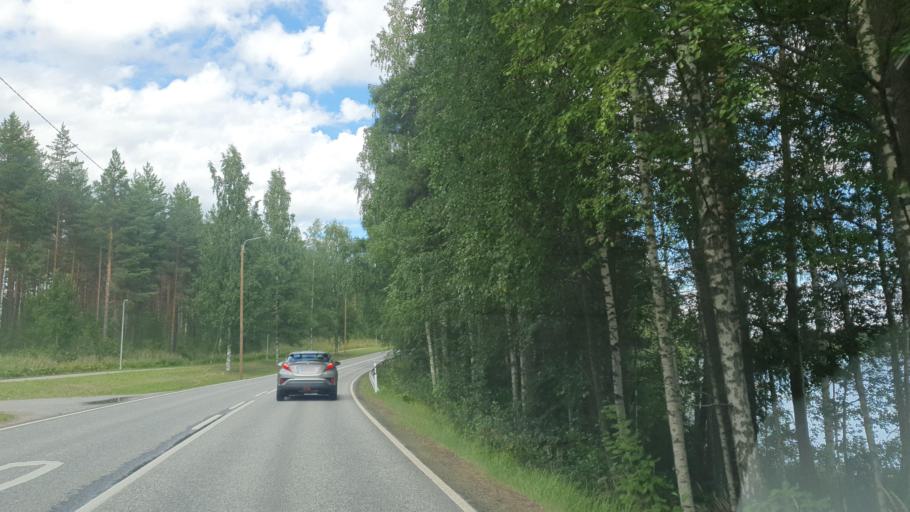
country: FI
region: Central Finland
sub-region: Jyvaeskylae
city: Saeynaetsalo
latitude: 62.1435
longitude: 25.7445
